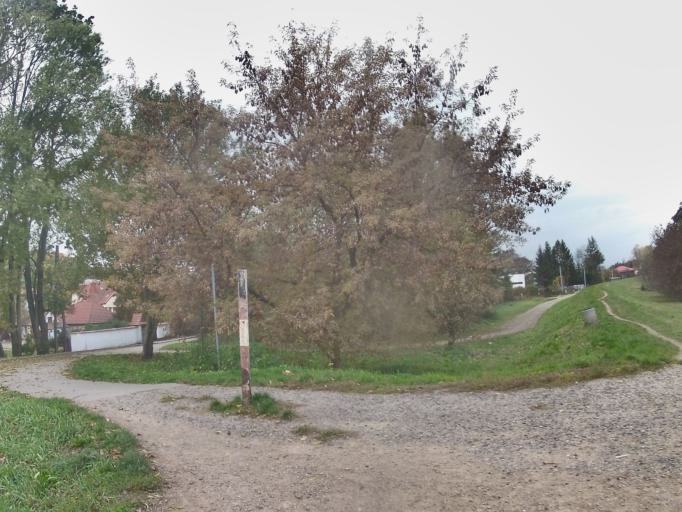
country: PL
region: Lesser Poland Voivodeship
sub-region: Krakow
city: Krakow
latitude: 50.0613
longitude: 19.8969
